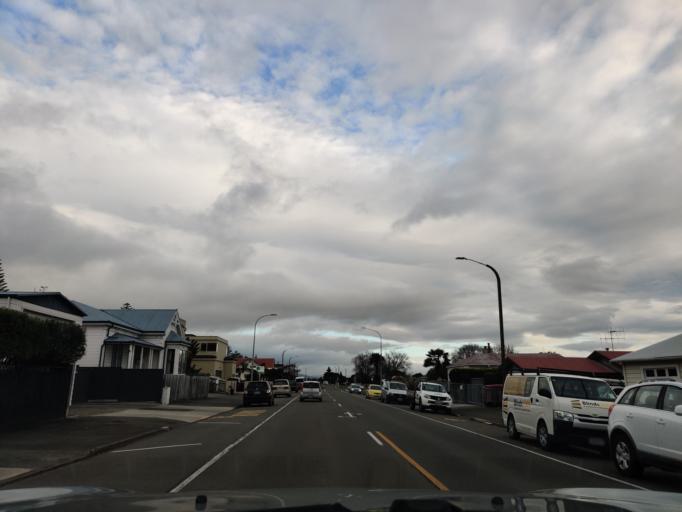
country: NZ
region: Hawke's Bay
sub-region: Napier City
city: Napier
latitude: -39.4987
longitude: 176.9178
